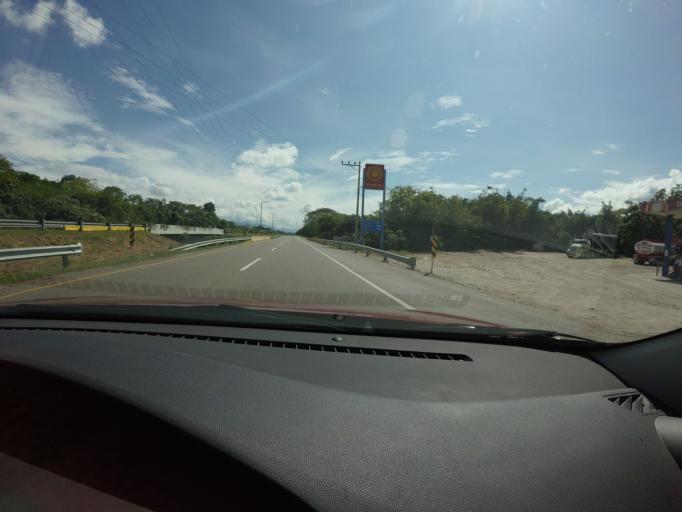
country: CO
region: Antioquia
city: Puerto Triunfo
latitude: 5.7318
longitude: -74.6237
